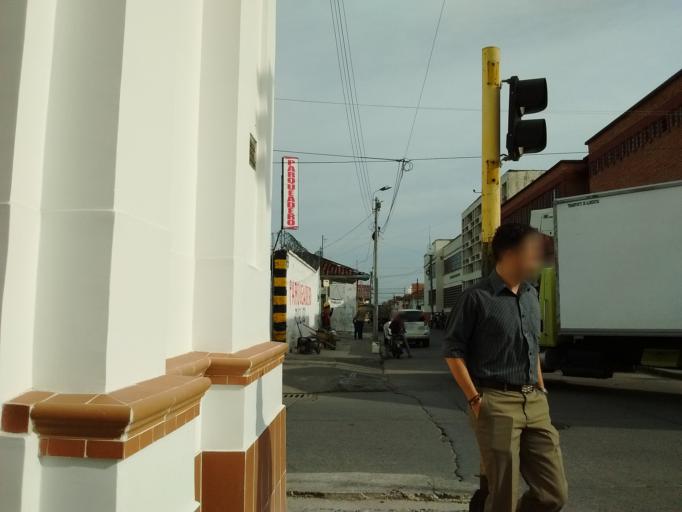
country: CO
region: Valle del Cauca
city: Tulua
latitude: 4.0862
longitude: -76.1976
